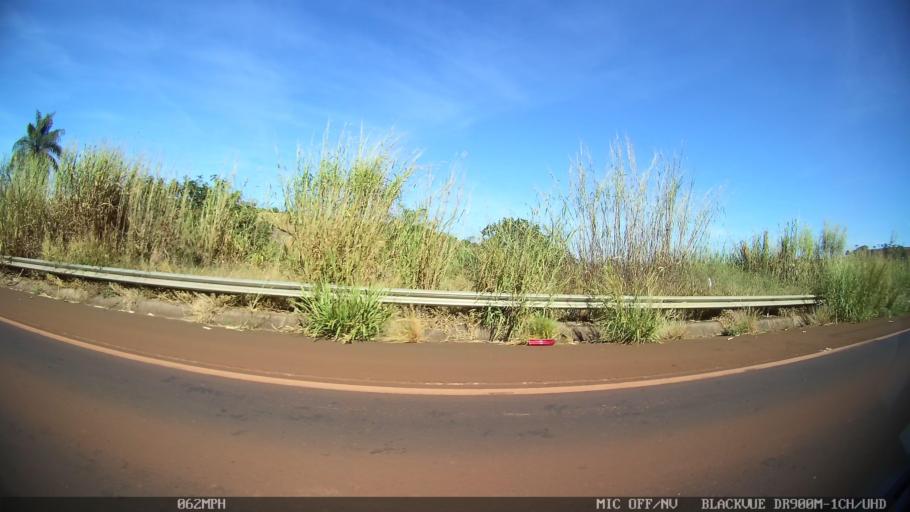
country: BR
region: Sao Paulo
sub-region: Sao Joaquim Da Barra
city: Sao Joaquim da Barra
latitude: -20.5532
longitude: -47.6747
